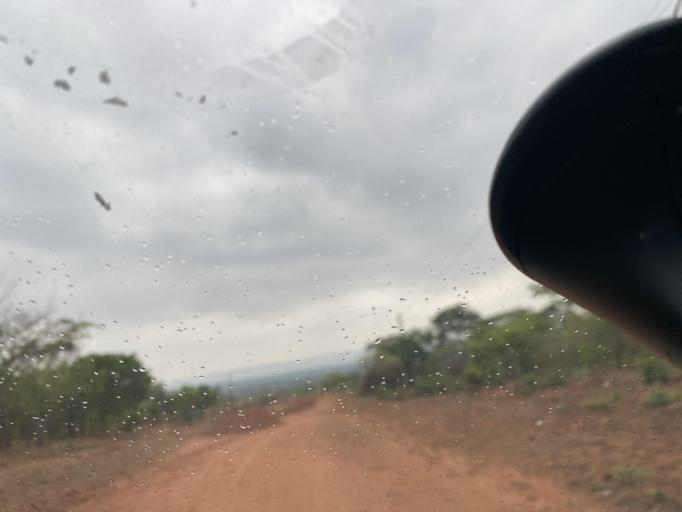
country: ZM
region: Lusaka
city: Chongwe
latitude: -15.1723
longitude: 28.7641
